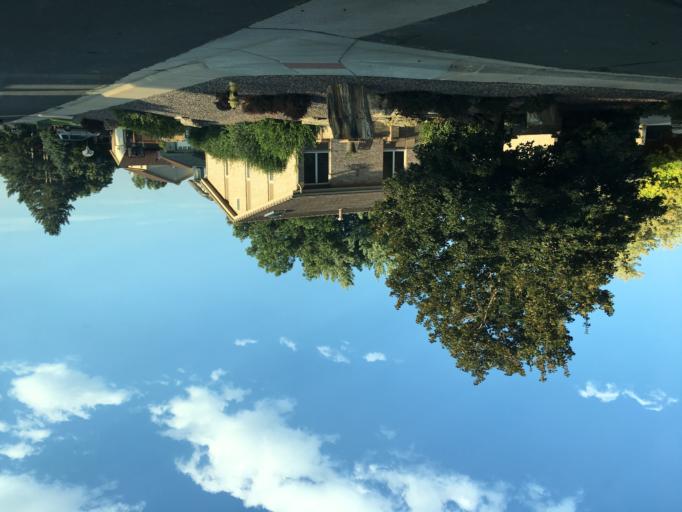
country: US
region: Colorado
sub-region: Jefferson County
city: Applewood
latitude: 39.7931
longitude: -105.1538
